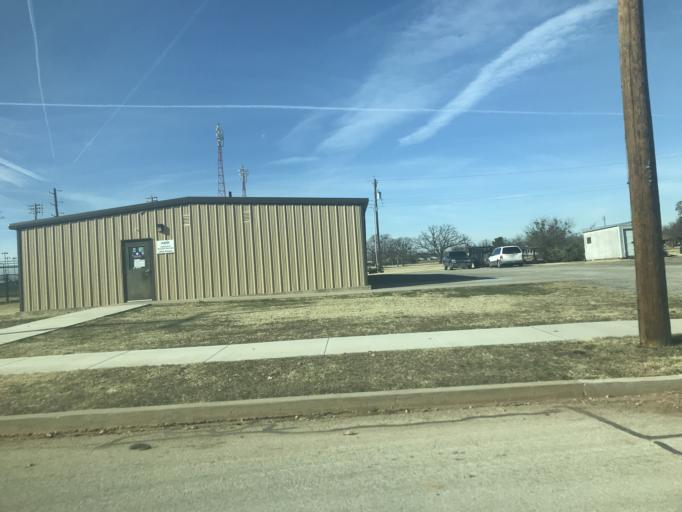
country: US
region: Texas
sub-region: Taylor County
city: Abilene
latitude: 32.4809
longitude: -99.7349
